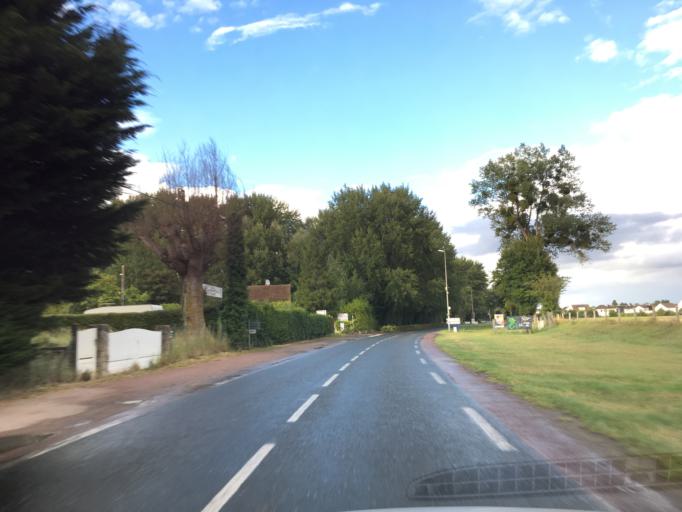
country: FR
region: Lower Normandy
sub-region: Departement du Calvados
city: Merville-Franceville-Plage
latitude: 49.2738
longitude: -0.2148
